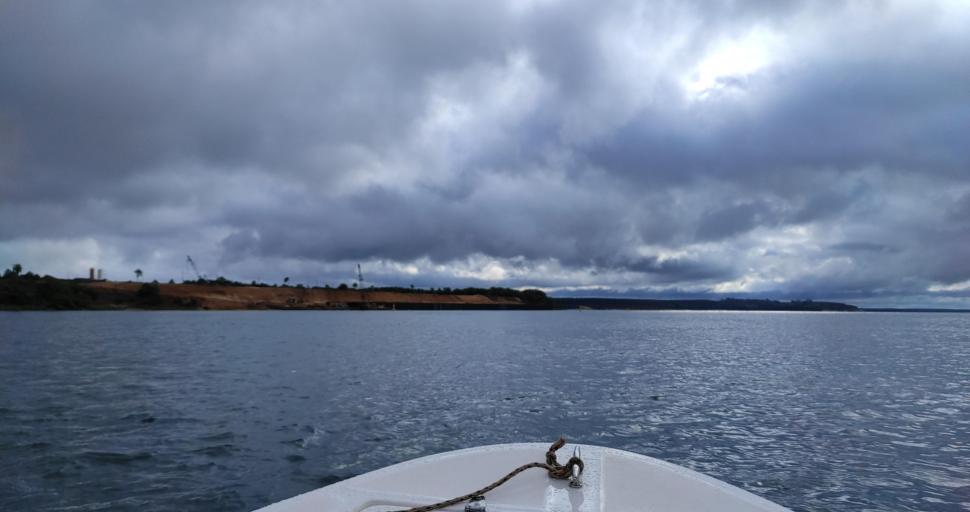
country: AR
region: Corrientes
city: Ituzaingo
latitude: -27.6068
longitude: -56.8308
